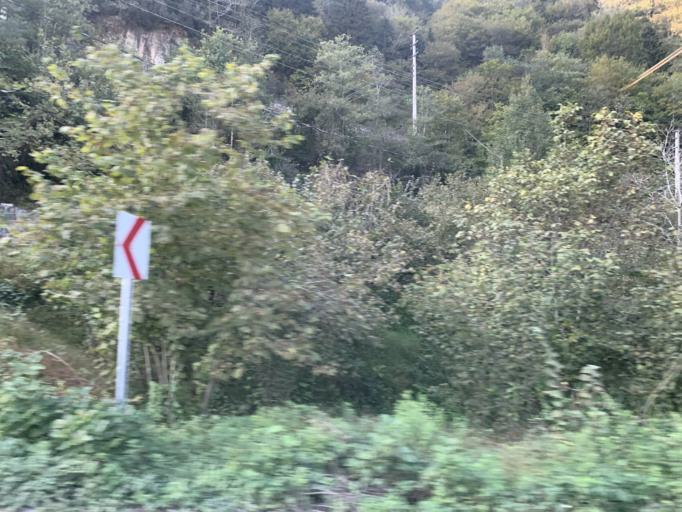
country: TR
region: Trabzon
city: Dernekpazari
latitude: 40.8337
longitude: 40.2704
